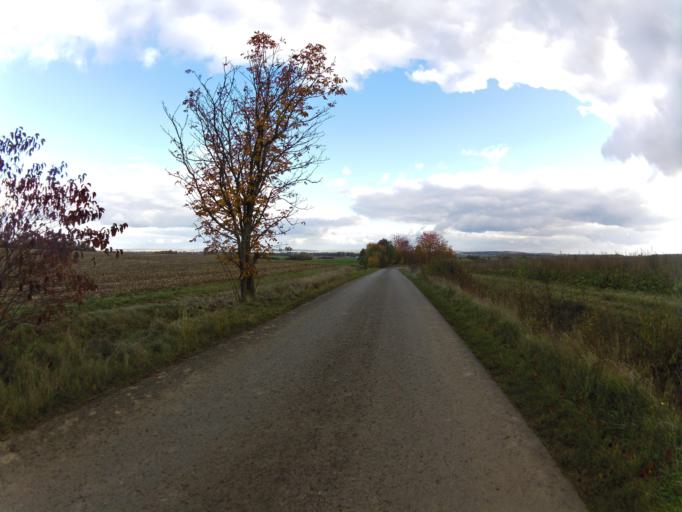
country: DE
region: Bavaria
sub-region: Regierungsbezirk Unterfranken
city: Kurnach
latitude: 49.8719
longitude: 9.9997
